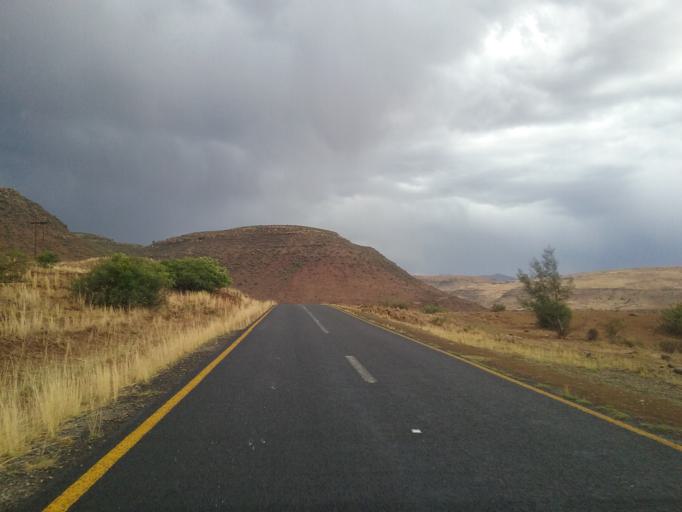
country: LS
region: Quthing
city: Quthing
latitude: -30.3496
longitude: 27.7234
